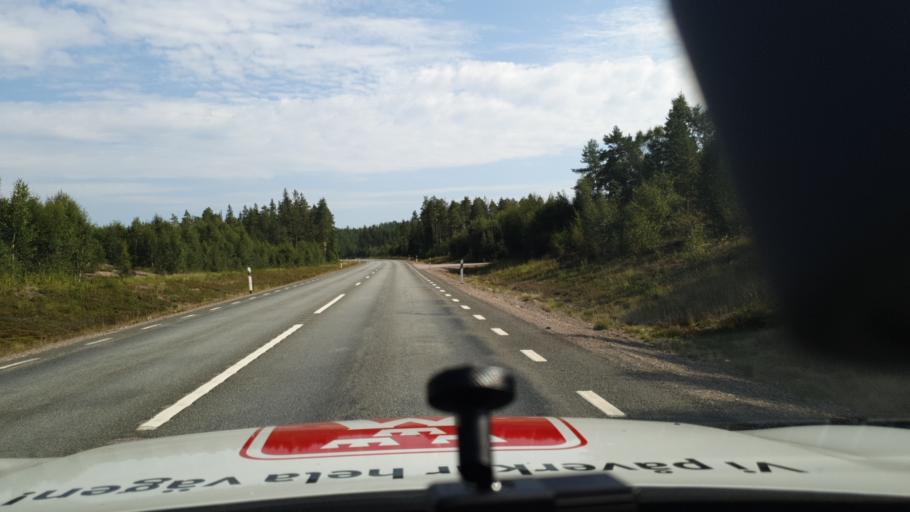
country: SE
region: Vaermland
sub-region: Hagfors Kommun
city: Ekshaerad
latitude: 60.4992
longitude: 13.4193
